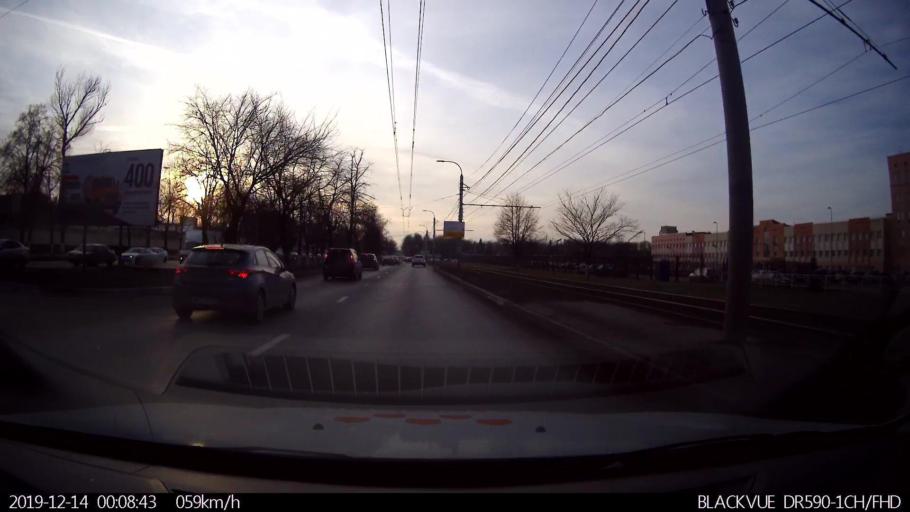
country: RU
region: Nizjnij Novgorod
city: Gorbatovka
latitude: 56.2481
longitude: 43.8781
